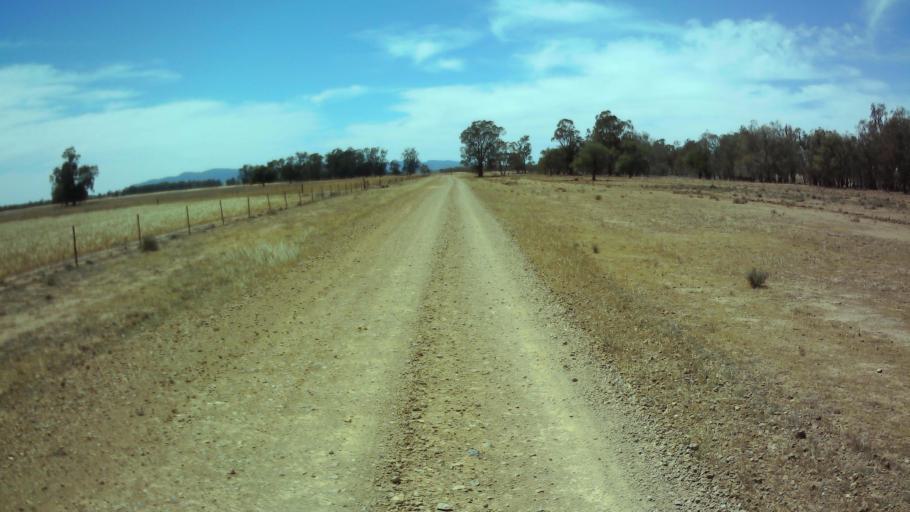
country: AU
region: New South Wales
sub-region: Weddin
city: Grenfell
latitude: -33.8608
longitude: 147.7547
